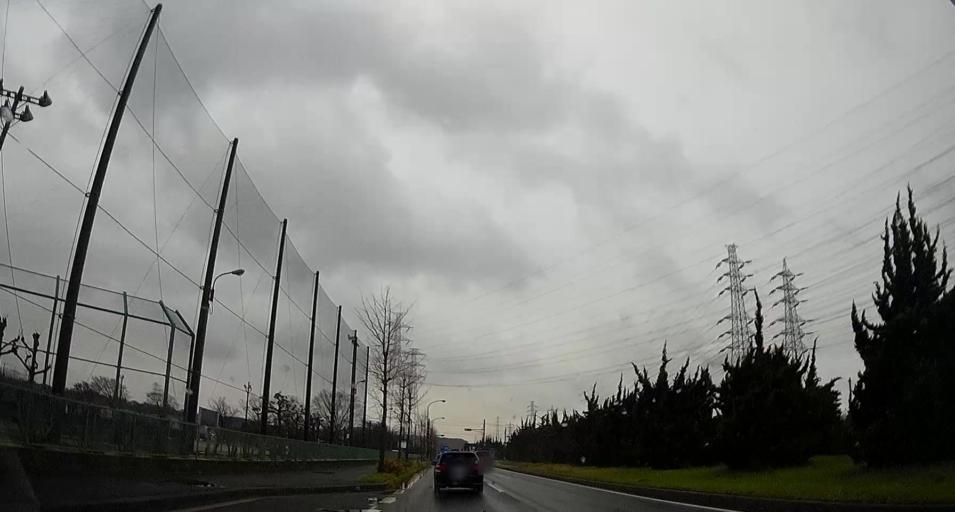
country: JP
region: Chiba
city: Ichihara
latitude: 35.4751
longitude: 140.0310
